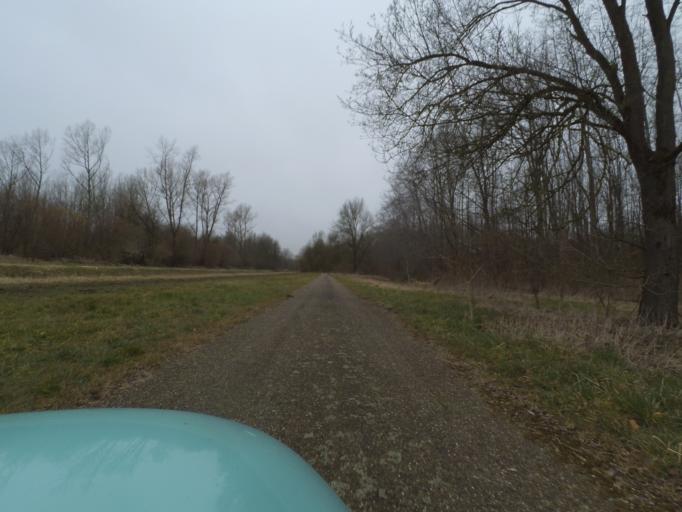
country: NL
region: Gelderland
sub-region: Gemeente Harderwijk
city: Harderwijk
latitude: 52.3961
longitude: 5.6324
